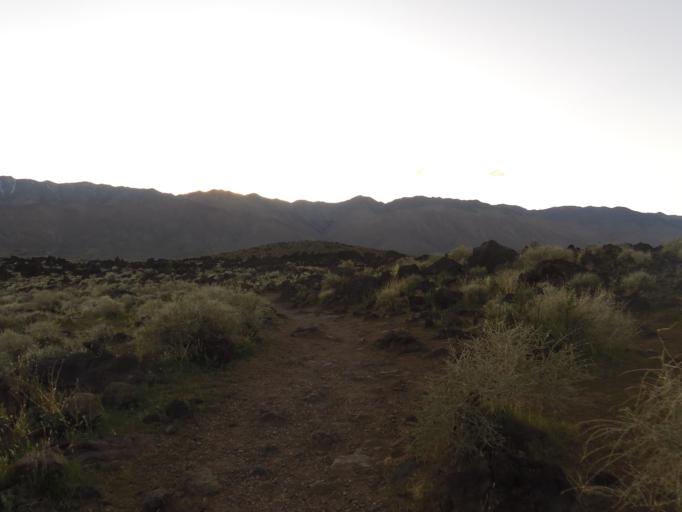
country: US
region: California
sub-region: Kern County
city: Inyokern
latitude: 35.9715
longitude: -117.9101
